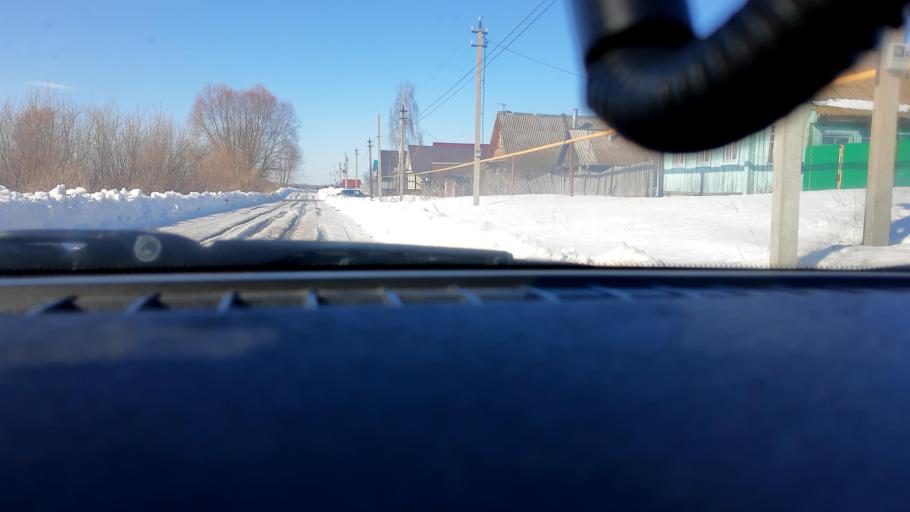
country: RU
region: Bashkortostan
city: Kabakovo
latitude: 54.7435
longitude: 56.1931
